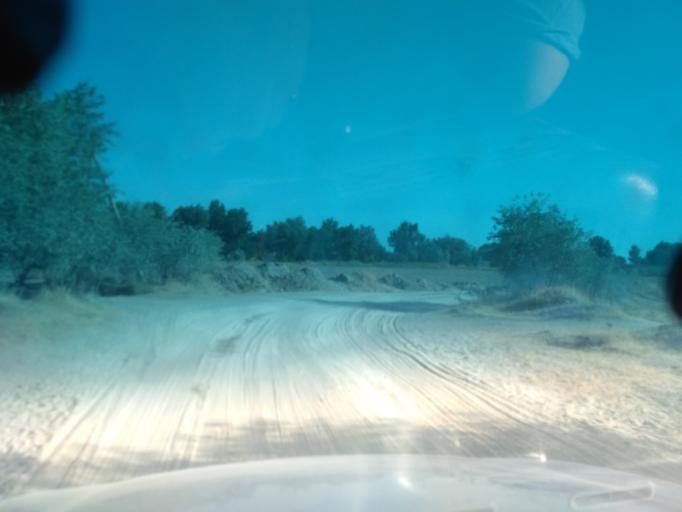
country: TJ
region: Viloyati Sughd
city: Buston
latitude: 40.5560
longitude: 69.0754
